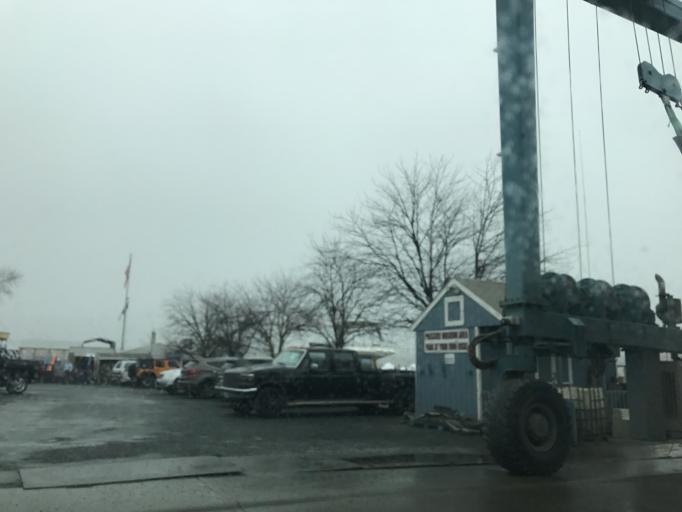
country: US
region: Maryland
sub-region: Baltimore County
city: Dundalk
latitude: 39.2508
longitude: -76.4897
